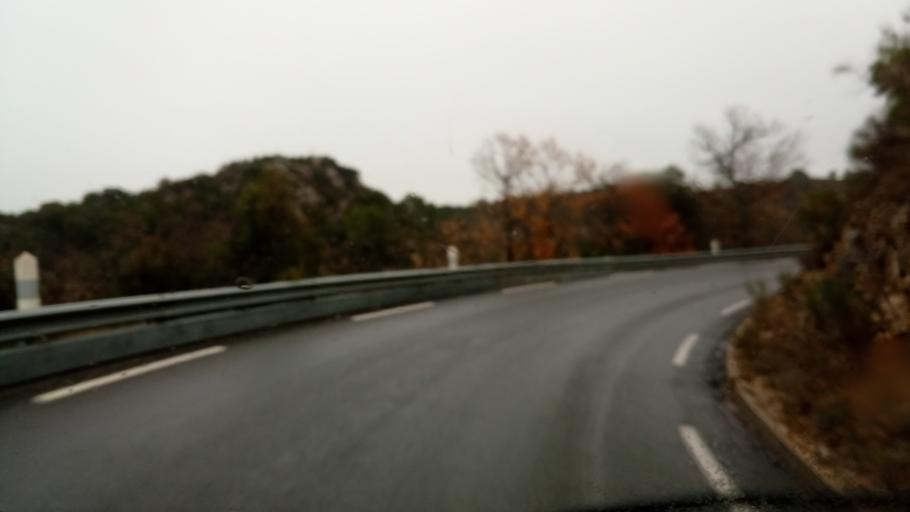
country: FR
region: Provence-Alpes-Cote d'Azur
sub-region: Departement du Var
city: Saint-Julien
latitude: 43.7023
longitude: 5.8814
